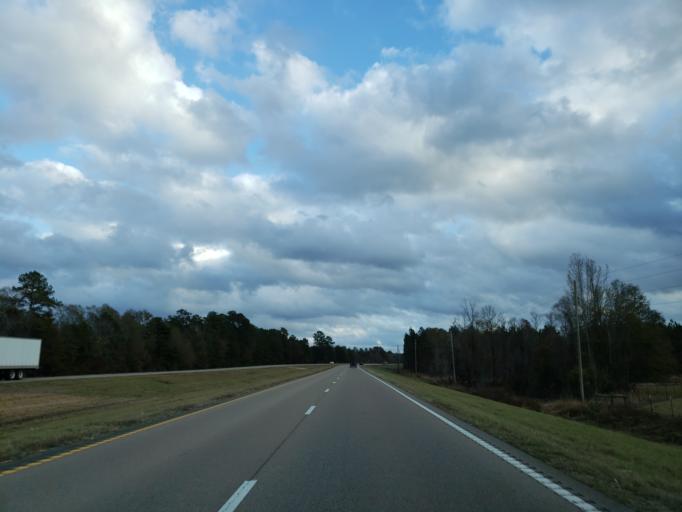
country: US
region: Mississippi
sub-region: Perry County
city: New Augusta
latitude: 31.1400
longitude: -88.8625
